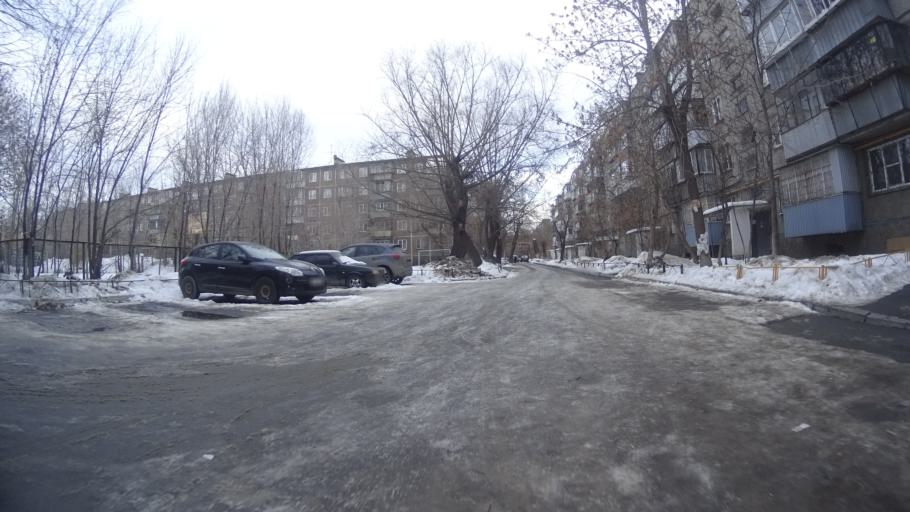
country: RU
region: Chelyabinsk
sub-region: Gorod Chelyabinsk
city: Chelyabinsk
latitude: 55.1386
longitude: 61.4045
